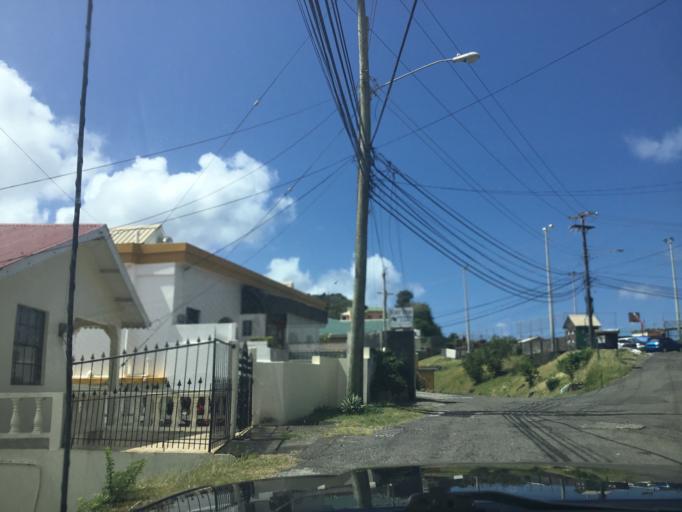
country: VC
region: Saint George
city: Kingstown Park
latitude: 13.1606
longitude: -61.2379
